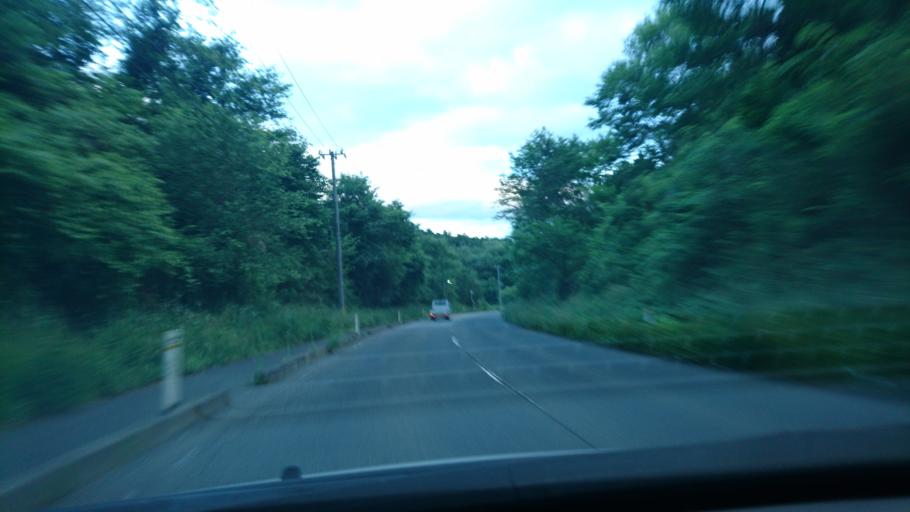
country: JP
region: Iwate
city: Ichinoseki
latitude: 38.7828
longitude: 141.0581
